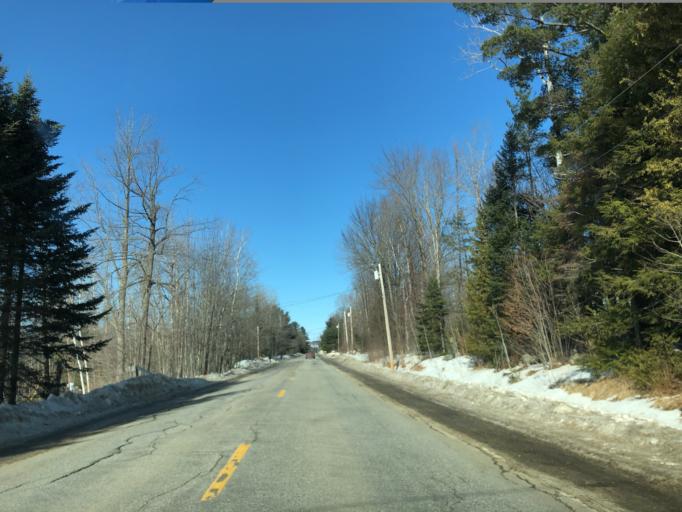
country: US
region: Maine
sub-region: Oxford County
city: Buckfield
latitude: 44.2476
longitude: -70.3371
